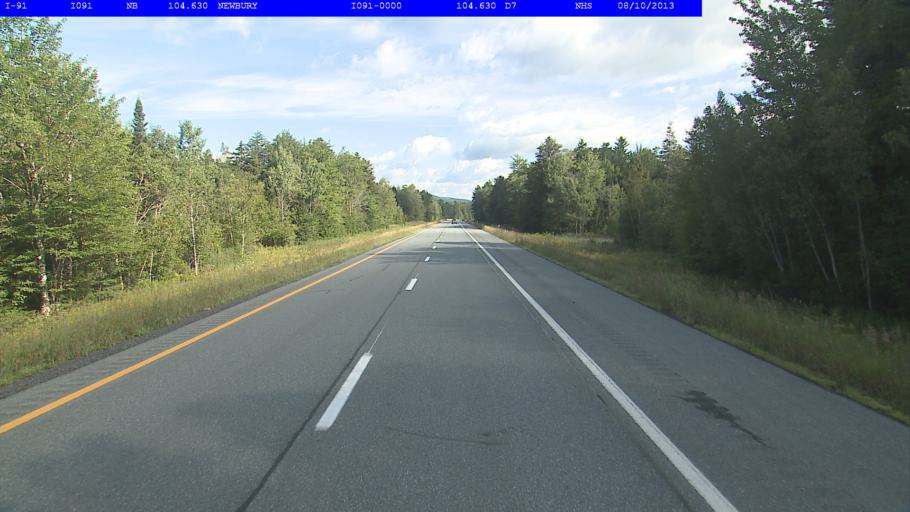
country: US
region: New Hampshire
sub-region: Grafton County
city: Haverhill
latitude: 44.0800
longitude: -72.1118
